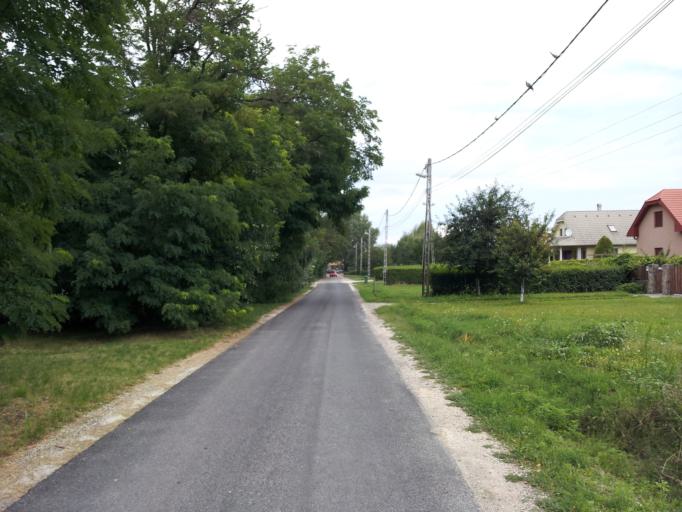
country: HU
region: Pest
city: Rackeve
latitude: 47.1847
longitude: 18.9564
